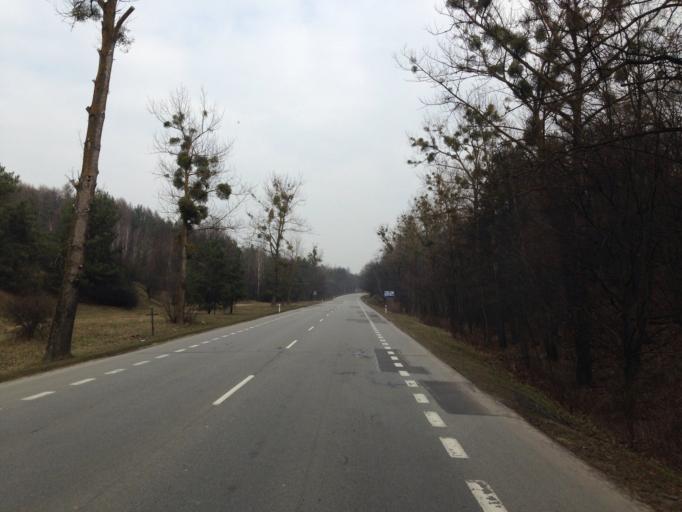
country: PL
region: Pomeranian Voivodeship
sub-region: Powiat tczewski
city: Gniew
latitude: 53.8140
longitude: 18.7937
